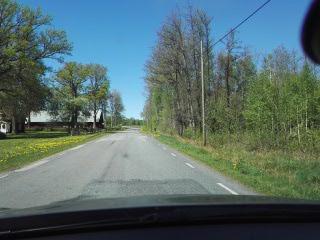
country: SE
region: Kronoberg
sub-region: Vaxjo Kommun
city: Rottne
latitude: 57.0836
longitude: 14.8192
